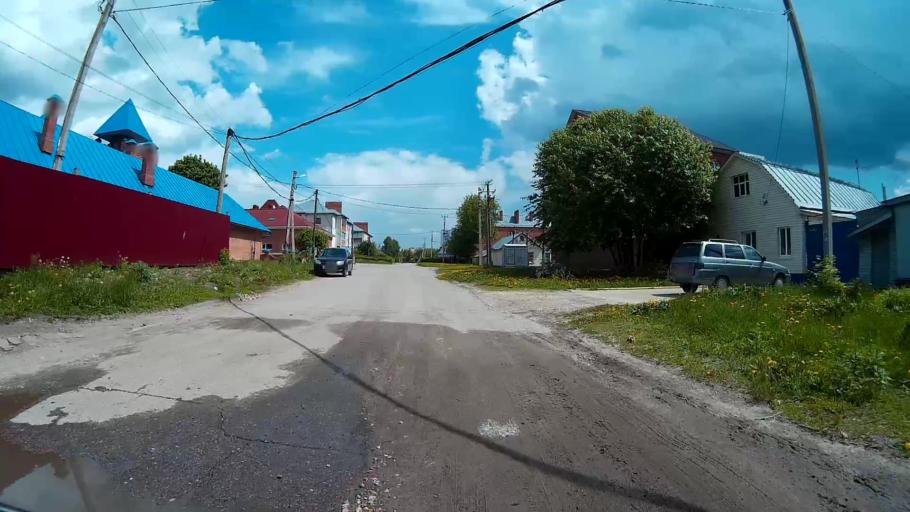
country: RU
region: Ulyanovsk
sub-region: Ulyanovskiy Rayon
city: Ulyanovsk
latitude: 54.3377
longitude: 48.3843
